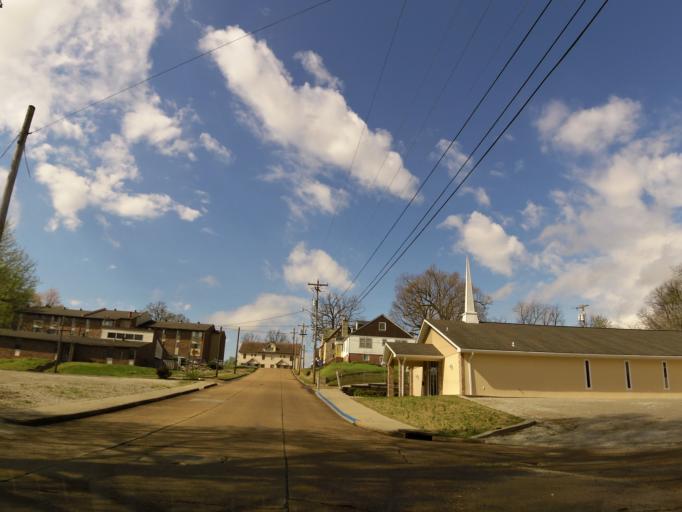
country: US
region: Missouri
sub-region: Butler County
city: Poplar Bluff
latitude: 36.7617
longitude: -90.3935
